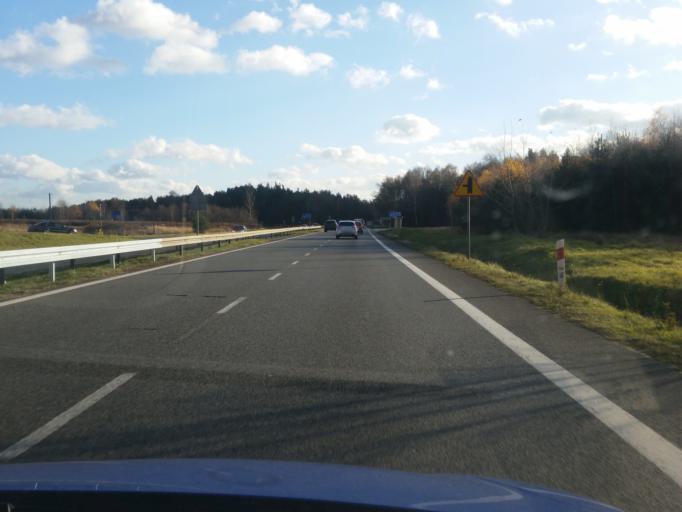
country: PL
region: Silesian Voivodeship
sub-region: Powiat myszkowski
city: Kozieglowy
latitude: 50.5352
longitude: 19.1886
